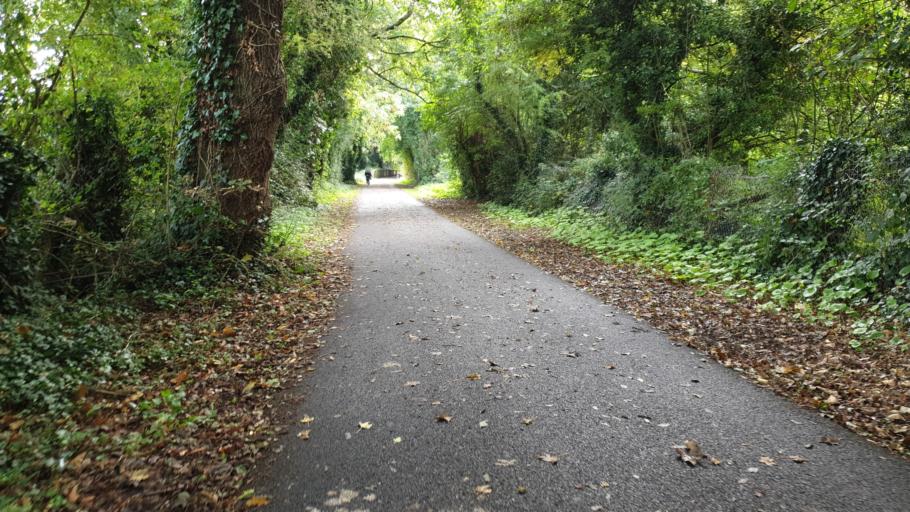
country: IE
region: Munster
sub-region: County Cork
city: Cork
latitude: 51.8982
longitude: -8.4225
